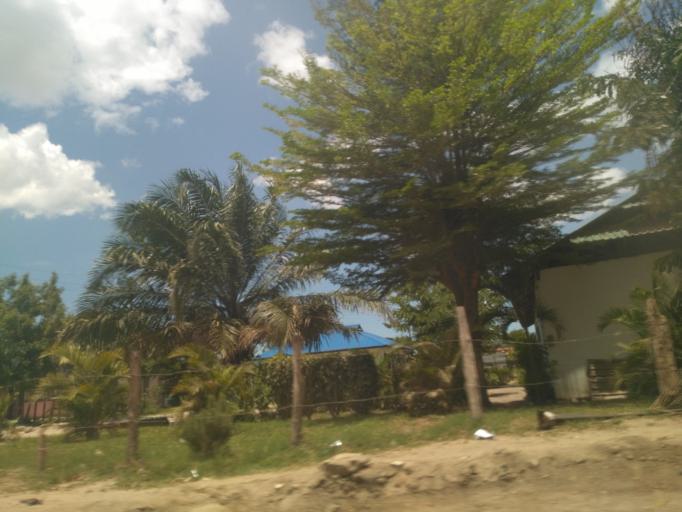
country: TZ
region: Dar es Salaam
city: Dar es Salaam
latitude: -6.8778
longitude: 39.2440
